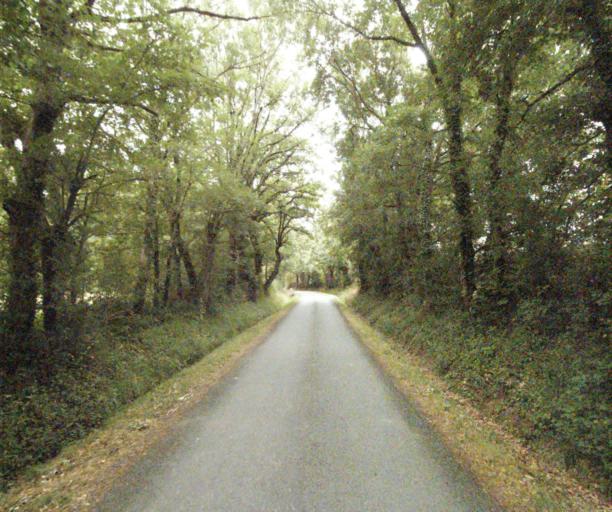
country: FR
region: Midi-Pyrenees
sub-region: Departement du Tarn
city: Soreze
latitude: 43.4752
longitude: 2.0654
